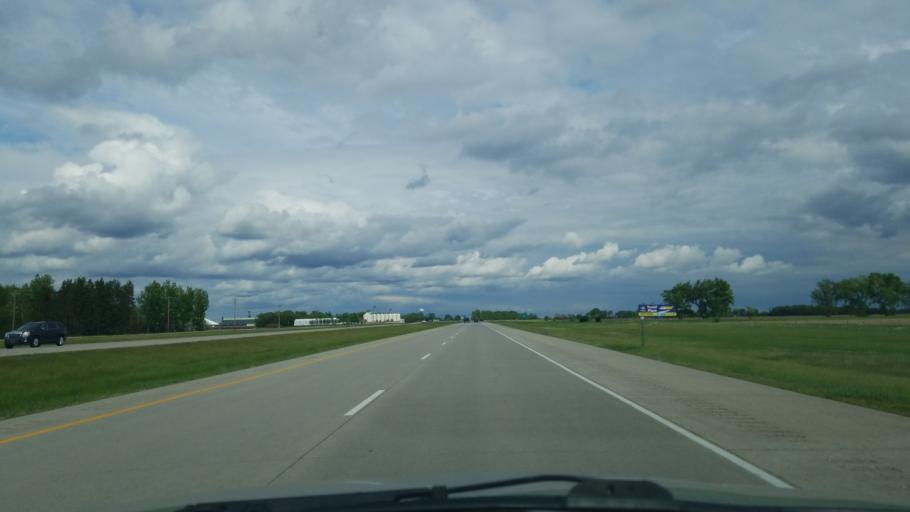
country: US
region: North Dakota
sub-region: Cass County
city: Casselton
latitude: 46.8759
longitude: -97.2462
